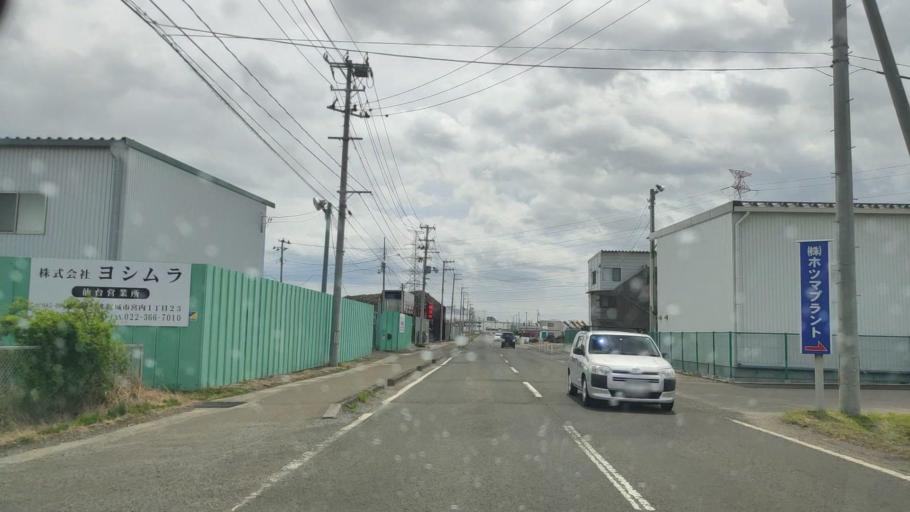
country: JP
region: Miyagi
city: Shiogama
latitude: 38.2815
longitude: 141.0079
